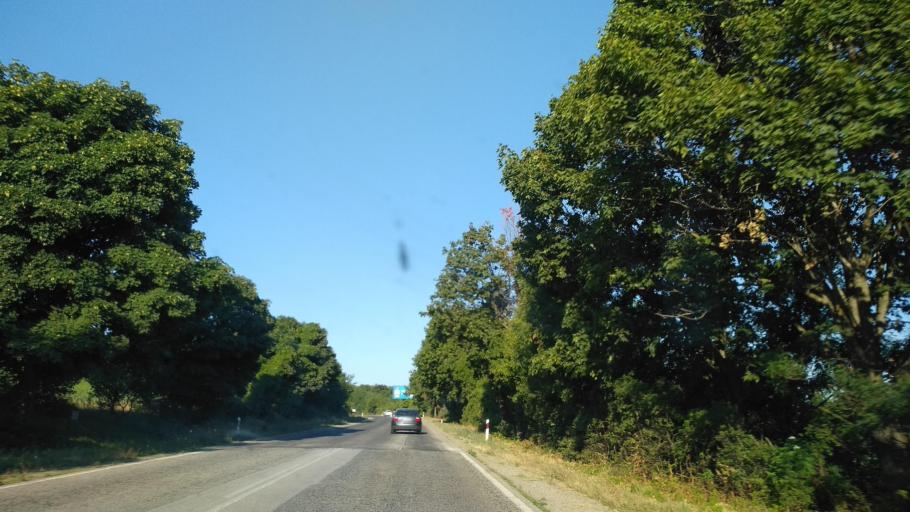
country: BG
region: Veliko Turnovo
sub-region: Obshtina Pavlikeni
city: Byala Cherkva
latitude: 43.0695
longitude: 25.3094
